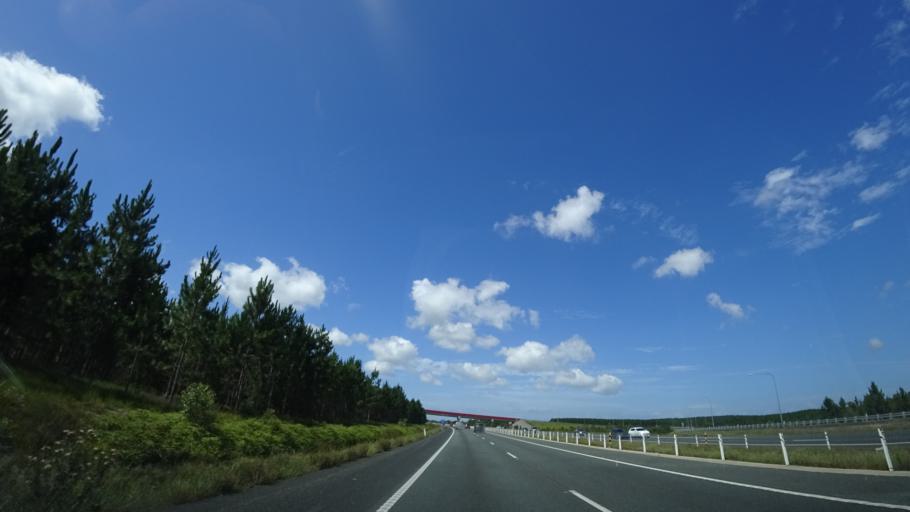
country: AU
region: Queensland
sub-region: Sunshine Coast
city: Little Mountain
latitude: -26.8540
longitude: 153.0246
